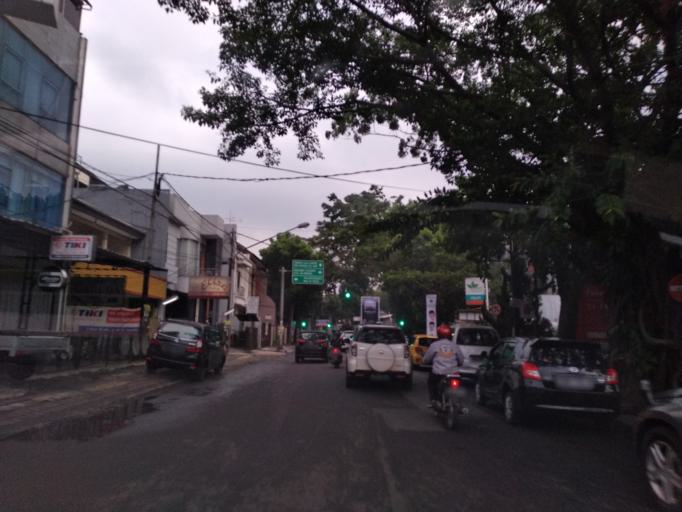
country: ID
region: West Java
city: Bandung
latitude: -6.9167
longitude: 107.6182
